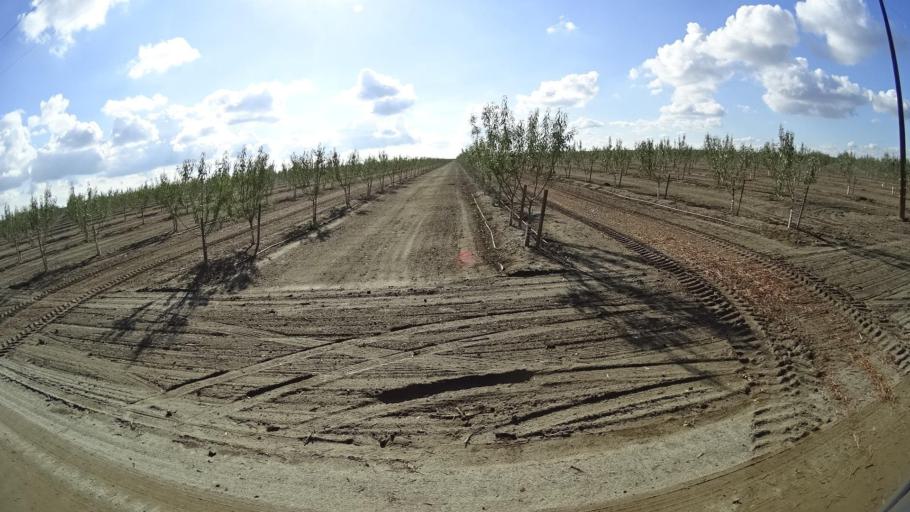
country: US
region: California
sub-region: Kern County
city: McFarland
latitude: 35.6599
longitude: -119.2288
